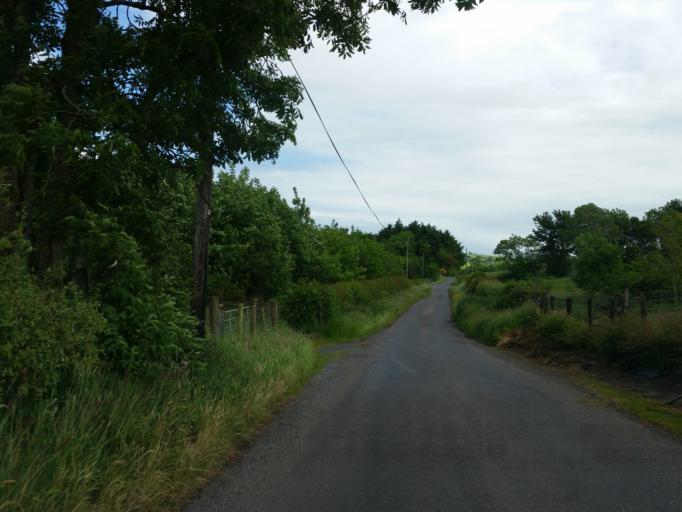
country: GB
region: Northern Ireland
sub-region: Omagh District
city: Omagh
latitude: 54.5473
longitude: -7.1252
